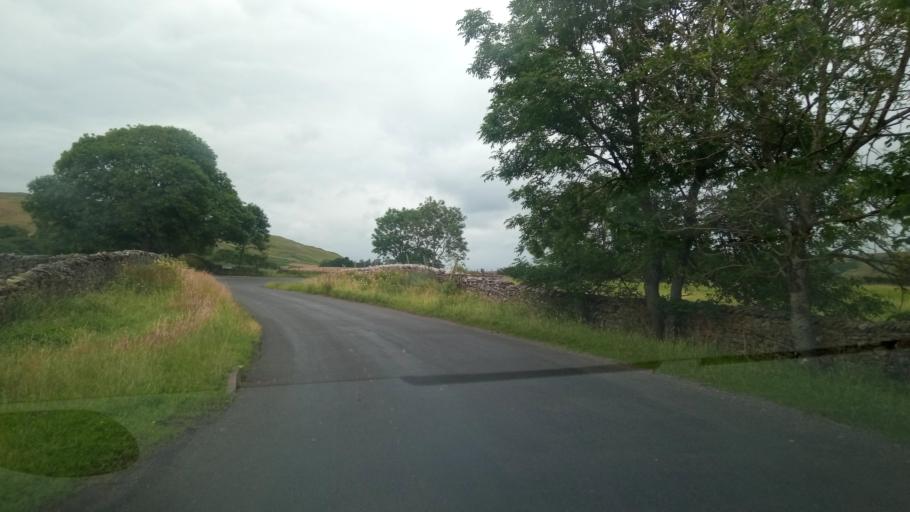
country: GB
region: England
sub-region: Cumbria
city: Kirkby Stephen
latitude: 54.4182
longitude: -2.3364
